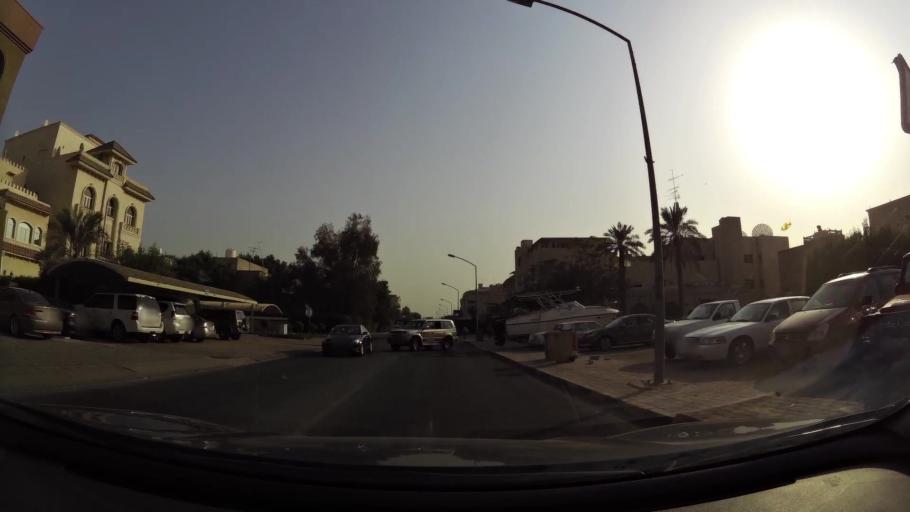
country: KW
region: Muhafazat Hawalli
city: Ar Rumaythiyah
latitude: 29.3216
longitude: 48.0771
